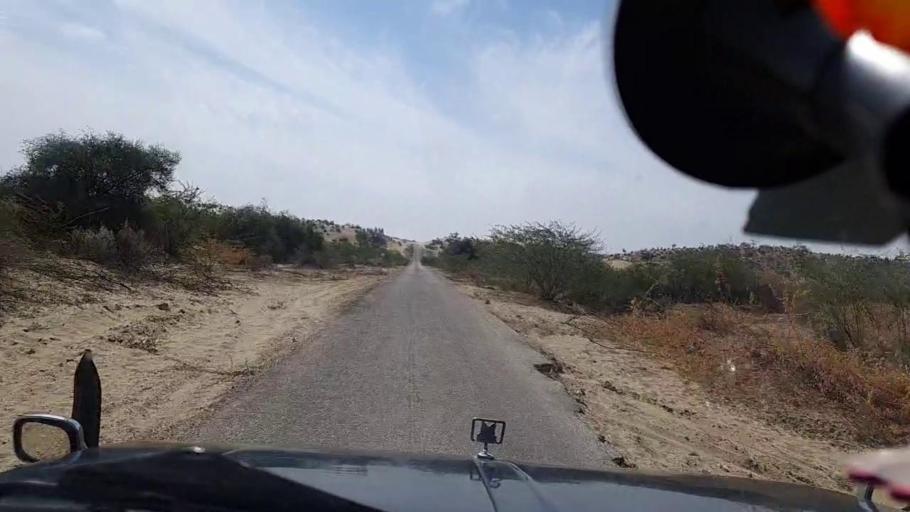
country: PK
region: Sindh
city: Diplo
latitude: 24.4169
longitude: 69.5845
